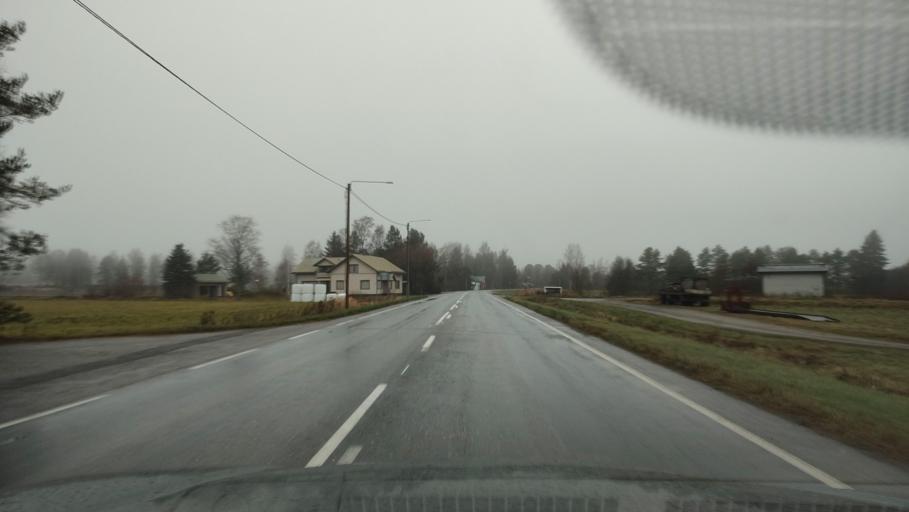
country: FI
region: Southern Ostrobothnia
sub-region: Suupohja
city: Karijoki
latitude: 62.1881
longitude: 21.7926
